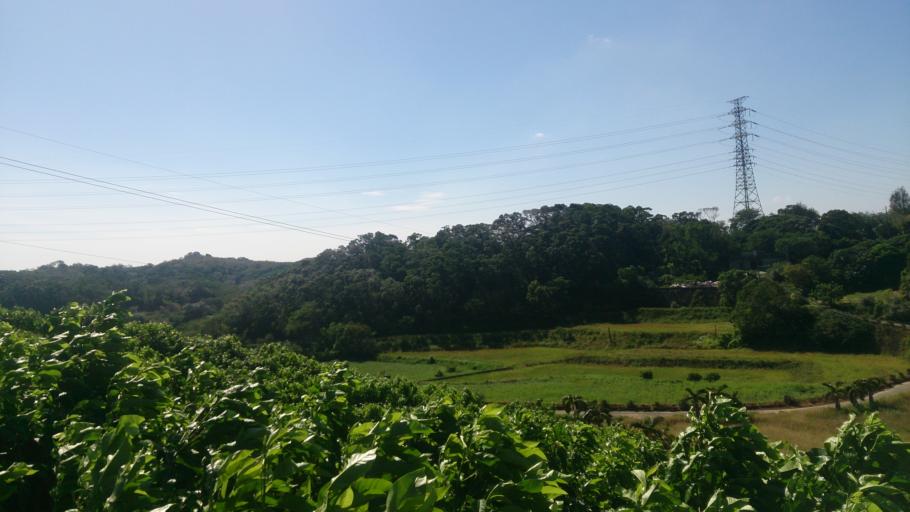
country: TW
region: Taiwan
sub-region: Hsinchu
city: Hsinchu
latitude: 24.7519
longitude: 120.9522
